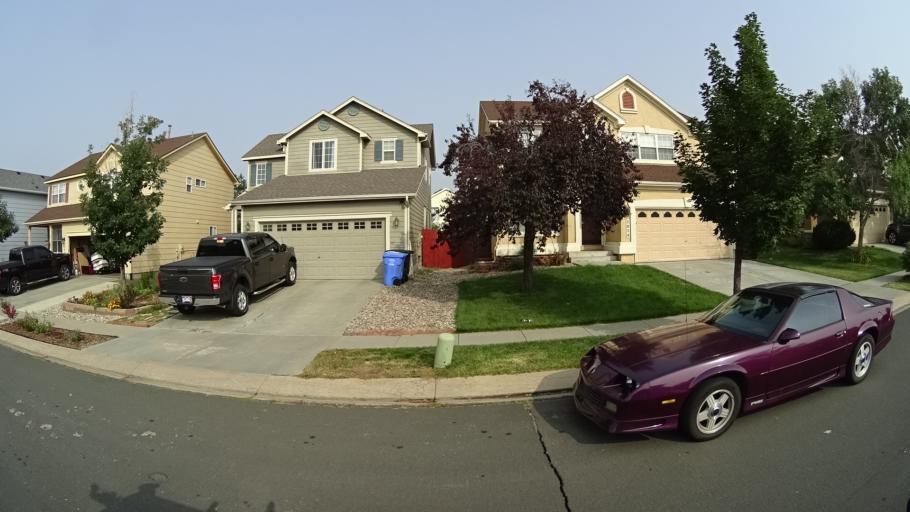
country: US
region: Colorado
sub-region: El Paso County
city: Cimarron Hills
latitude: 38.9334
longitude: -104.7256
